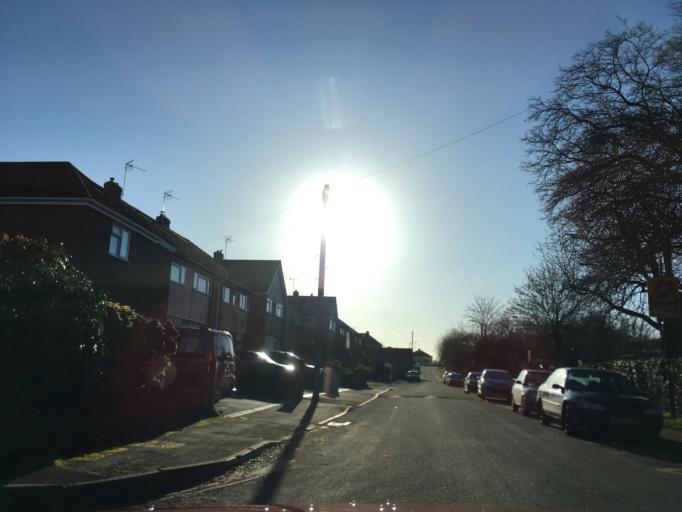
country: GB
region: England
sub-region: South Gloucestershire
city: Chipping Sodbury
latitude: 51.5373
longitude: -2.3933
